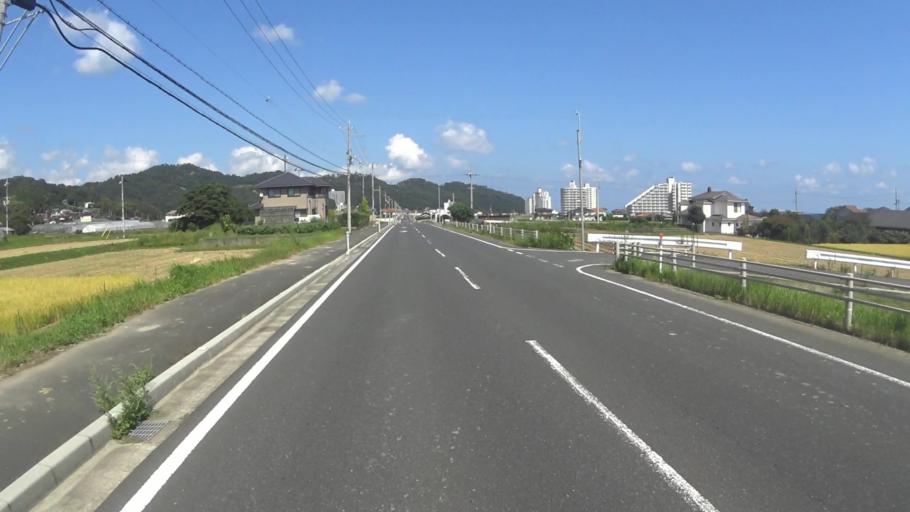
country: JP
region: Kyoto
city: Miyazu
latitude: 35.6068
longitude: 135.2240
